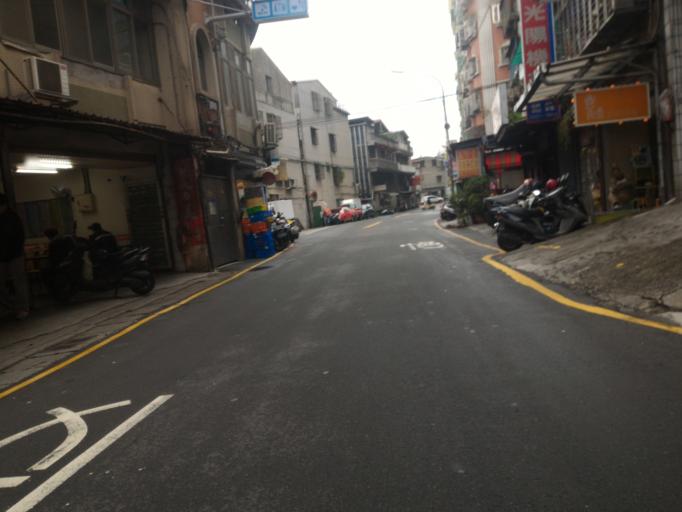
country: TW
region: Taipei
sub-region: Taipei
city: Banqiao
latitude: 25.0392
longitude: 121.4578
